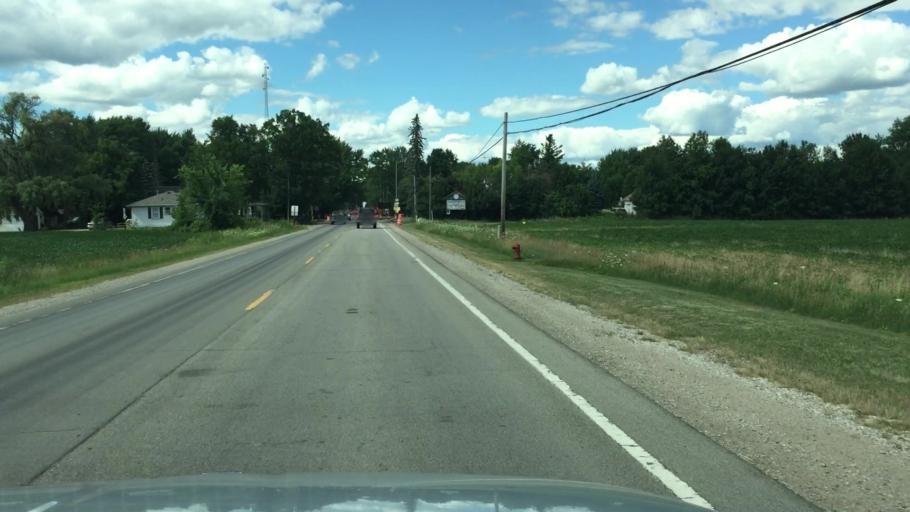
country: US
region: Michigan
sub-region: Saint Clair County
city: Capac
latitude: 43.0038
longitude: -82.9282
